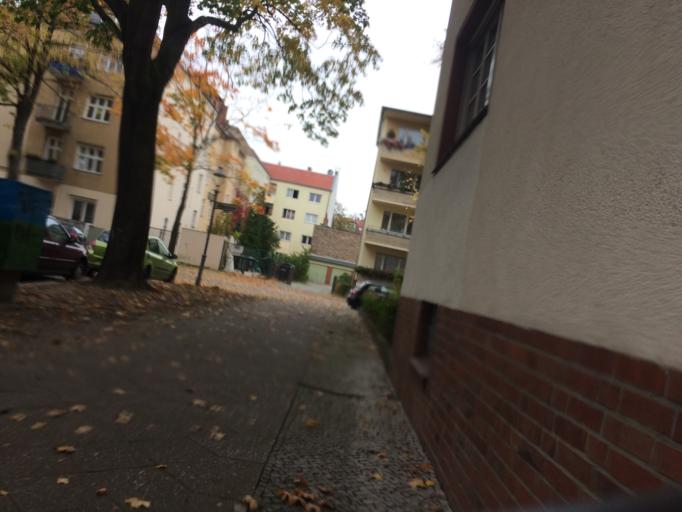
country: DE
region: Berlin
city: Wilhelmsruh
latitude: 52.5676
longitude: 13.3767
